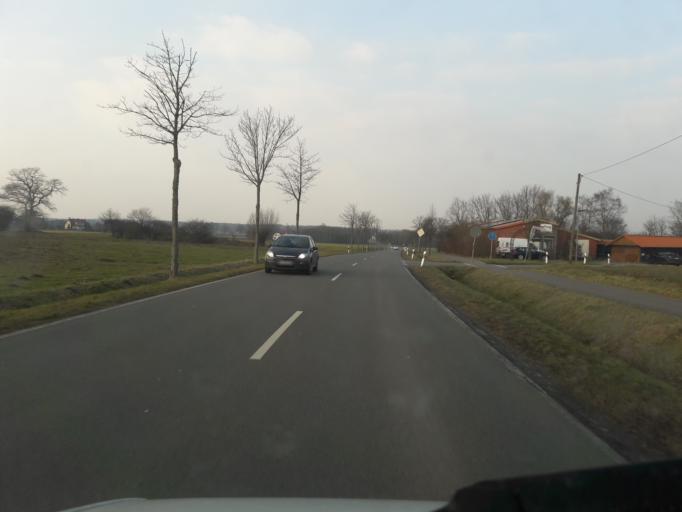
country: DE
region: North Rhine-Westphalia
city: Espelkamp
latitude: 52.3523
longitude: 8.6478
